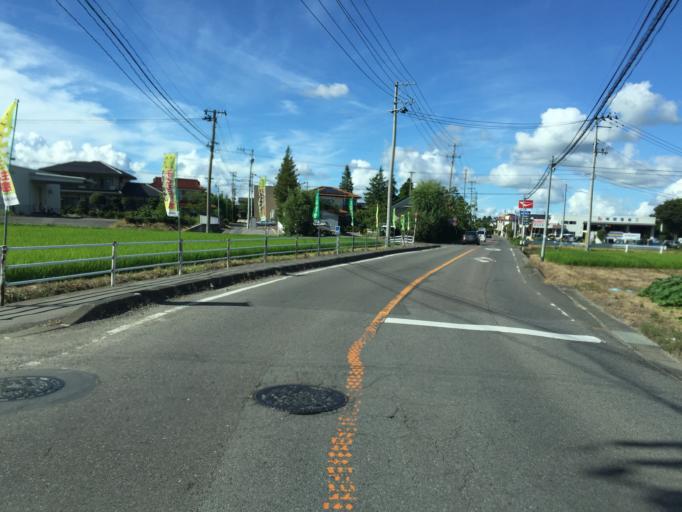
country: JP
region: Fukushima
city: Motomiya
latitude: 37.4949
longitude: 140.4015
